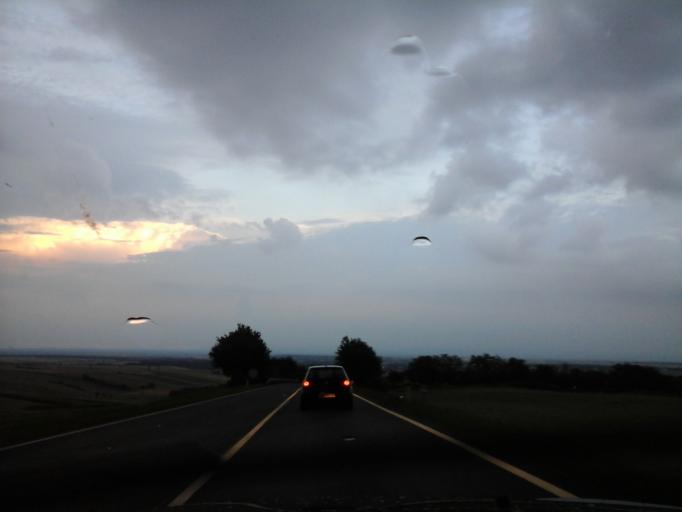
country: AT
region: Lower Austria
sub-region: Politischer Bezirk Ganserndorf
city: Zistersdorf
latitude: 48.5593
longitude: 16.7290
